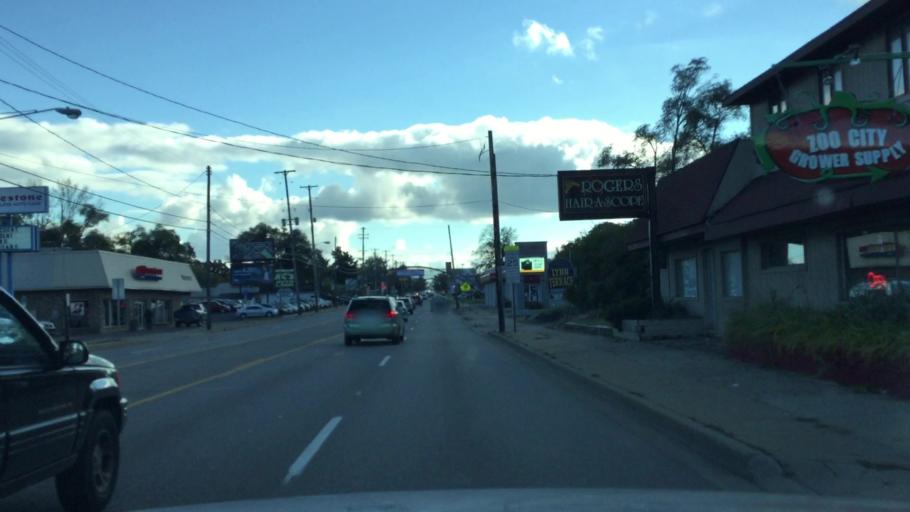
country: US
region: Michigan
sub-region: Kalamazoo County
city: Kalamazoo
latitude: 42.2565
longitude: -85.5897
